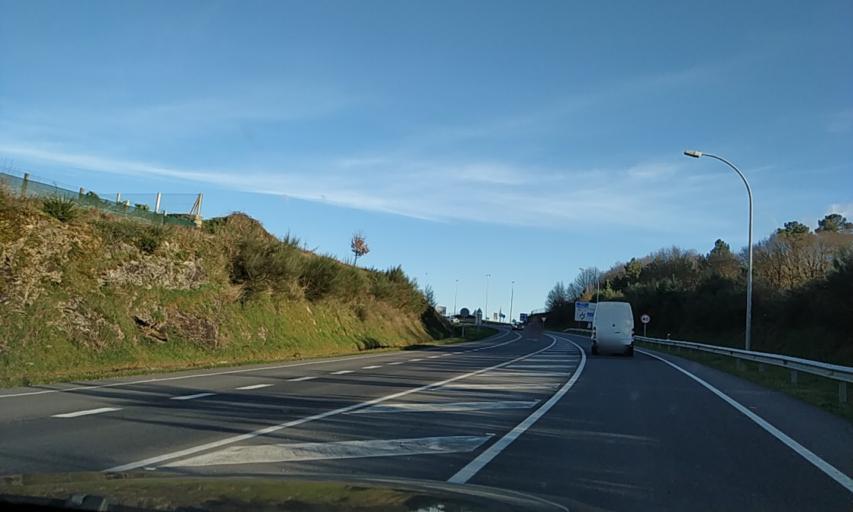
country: ES
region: Galicia
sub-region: Provincia de Pontevedra
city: Lalin
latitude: 42.6746
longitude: -8.1635
